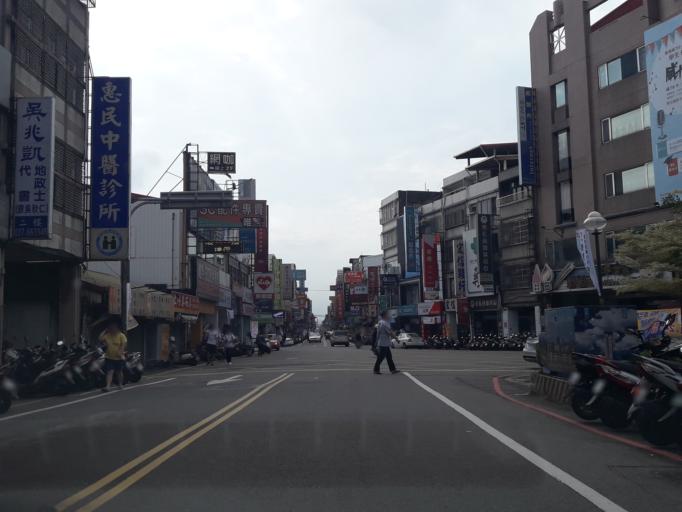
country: TW
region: Taiwan
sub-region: Hsinchu
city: Hsinchu
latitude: 24.6871
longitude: 120.9110
